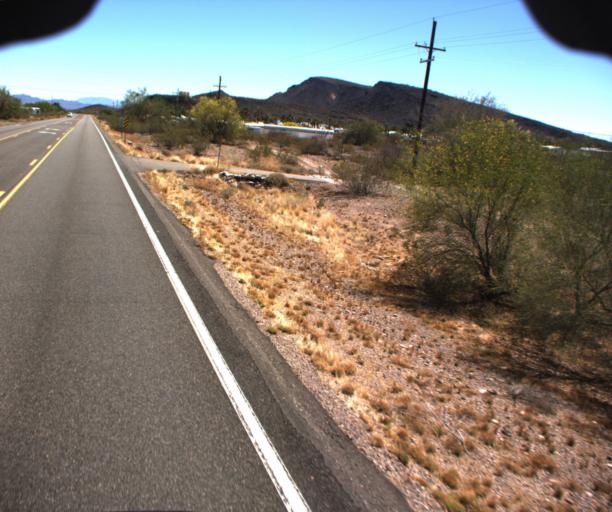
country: US
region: Arizona
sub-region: La Paz County
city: Quartzsite
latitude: 33.6779
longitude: -113.9514
